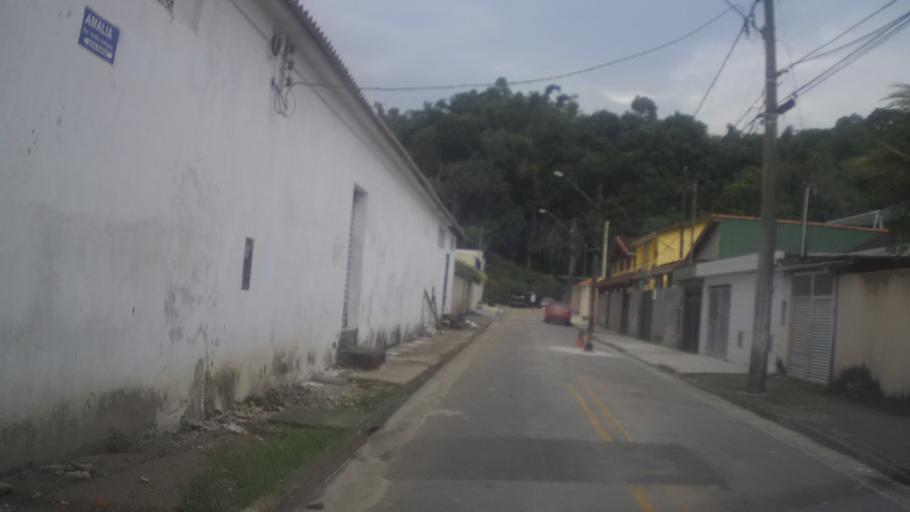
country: BR
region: Sao Paulo
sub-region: Santos
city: Santos
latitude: -23.9433
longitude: -46.3477
